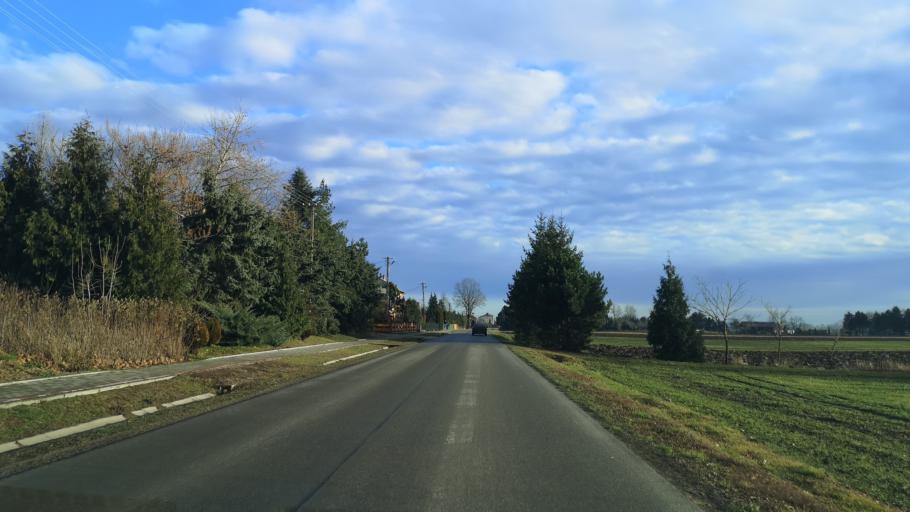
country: PL
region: Subcarpathian Voivodeship
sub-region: Powiat lezajski
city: Piskorowice
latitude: 50.2442
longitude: 22.5099
